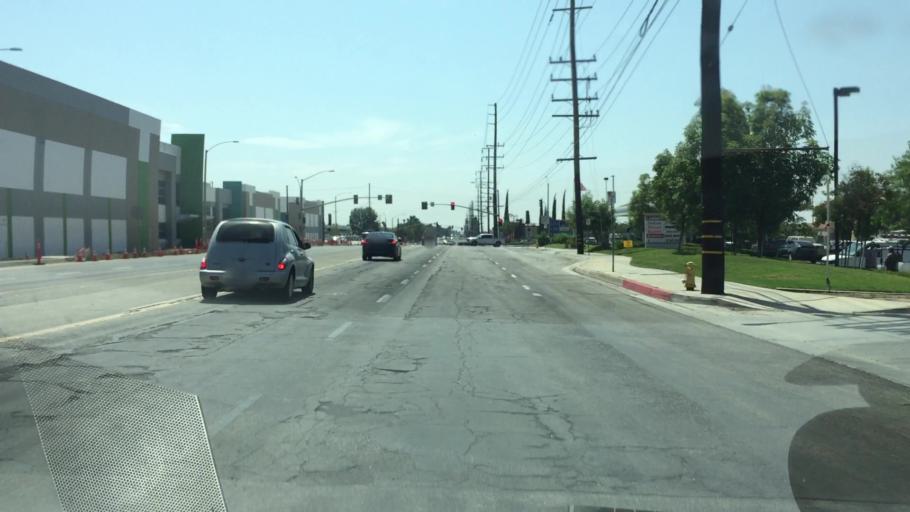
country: US
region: California
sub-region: Orange County
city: La Habra
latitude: 33.9247
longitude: -117.9294
